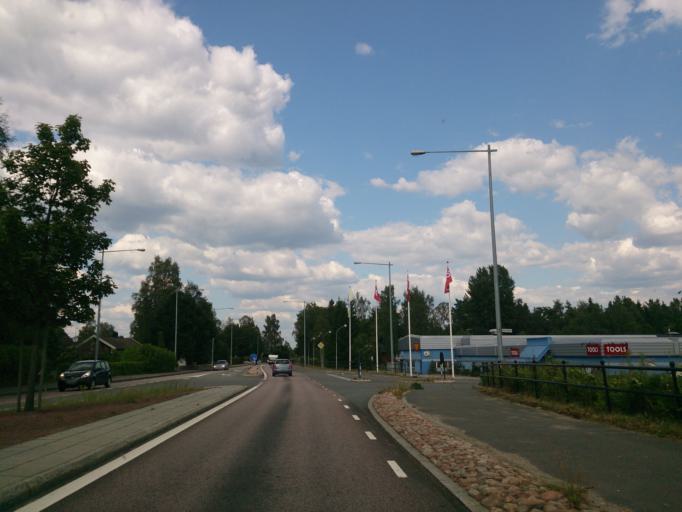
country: SE
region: Joenkoeping
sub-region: Gislaveds Kommun
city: Smalandsstenar
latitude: 57.1523
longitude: 13.3999
